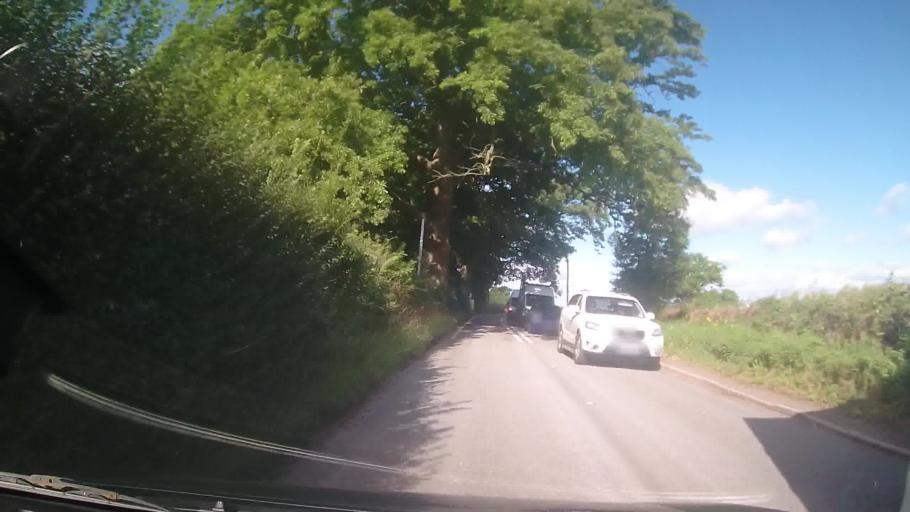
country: GB
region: England
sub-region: Shropshire
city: Bicton
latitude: 52.7623
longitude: -2.7946
